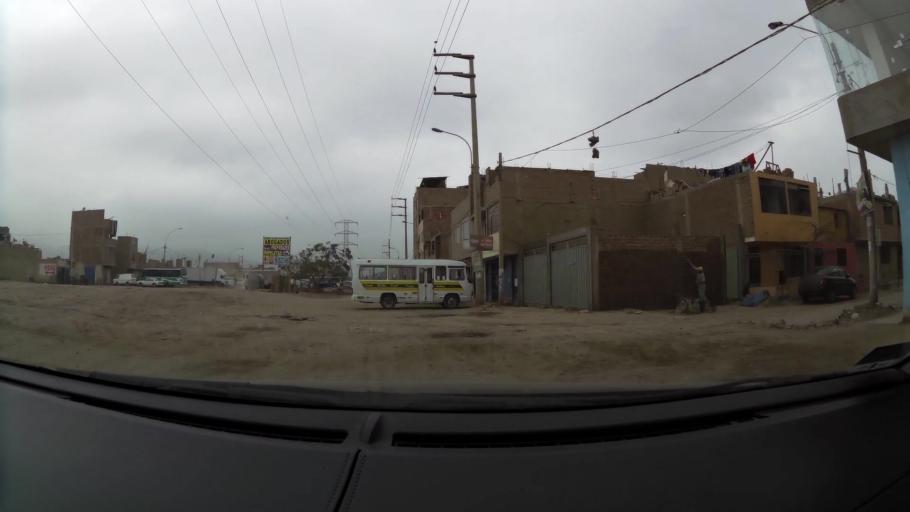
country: PE
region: Lima
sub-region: Lima
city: Independencia
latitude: -11.9715
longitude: -77.0902
